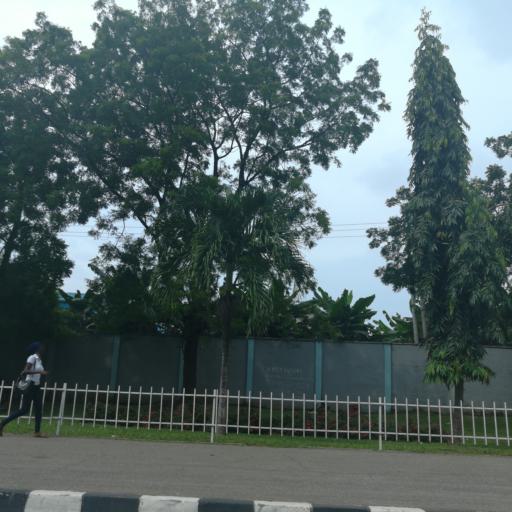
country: NG
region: Lagos
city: Ikeja
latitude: 6.6140
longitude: 3.3594
